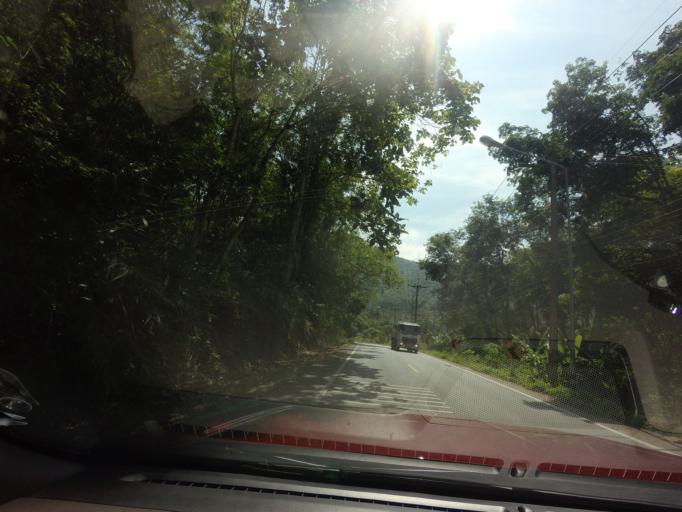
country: TH
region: Yala
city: Betong
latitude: 5.8262
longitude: 101.0784
